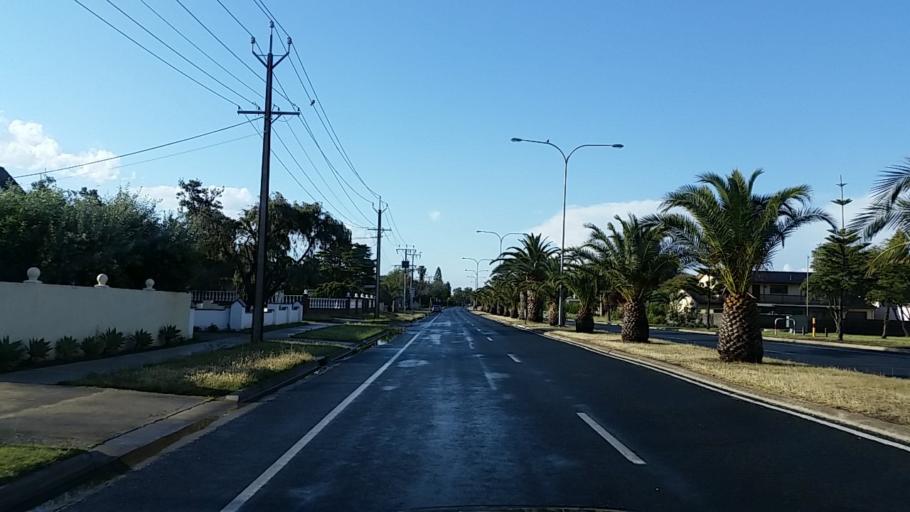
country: AU
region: South Australia
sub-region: Charles Sturt
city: Grange
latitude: -34.8857
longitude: 138.4865
